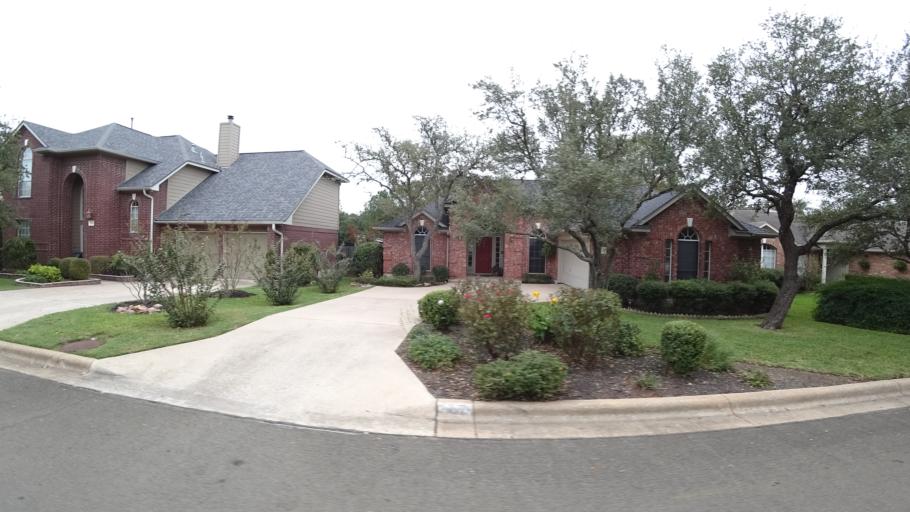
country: US
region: Texas
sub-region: Travis County
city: Shady Hollow
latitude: 30.2096
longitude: -97.8872
